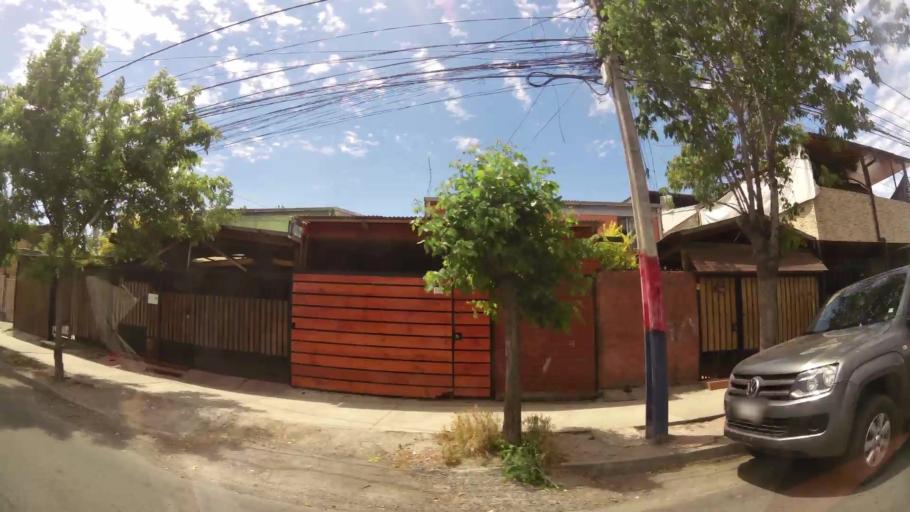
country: CL
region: Santiago Metropolitan
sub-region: Provincia de Santiago
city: La Pintana
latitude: -33.5651
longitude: -70.6351
